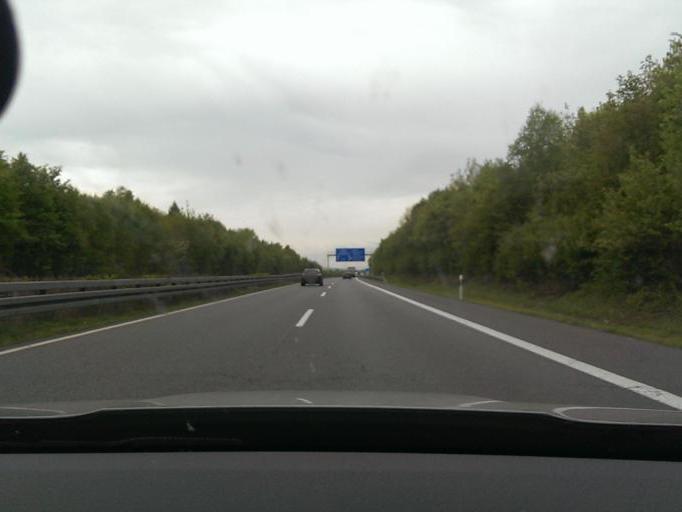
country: DE
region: Lower Saxony
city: Lehre
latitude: 52.3259
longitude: 10.7334
